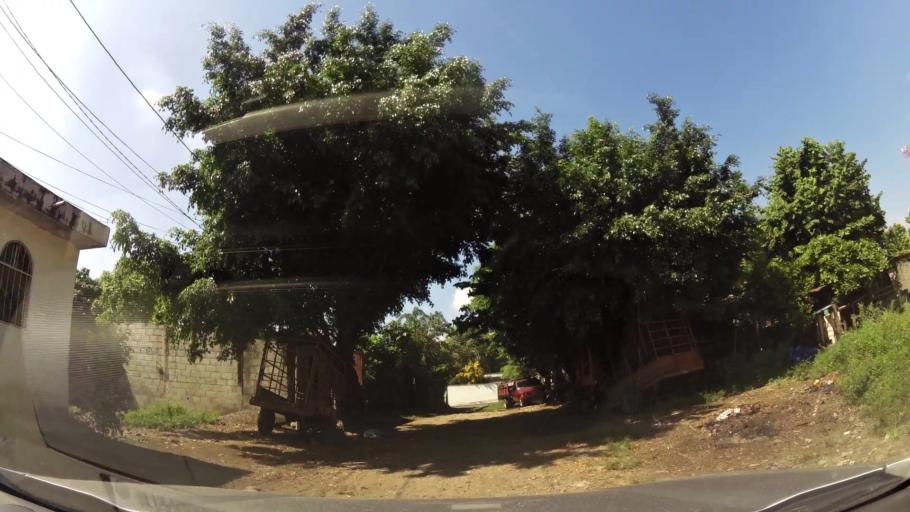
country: GT
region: Suchitepeque
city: Mazatenango
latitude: 14.5312
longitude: -91.4889
